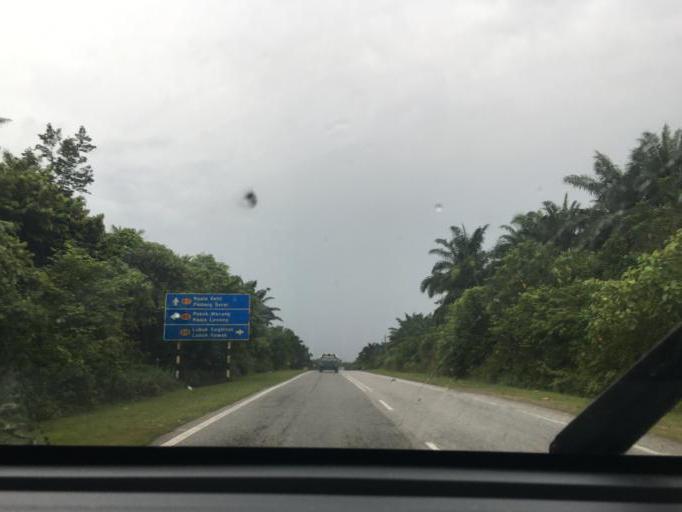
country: MY
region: Kedah
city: Sungai Petani
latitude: 5.6265
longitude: 100.6349
